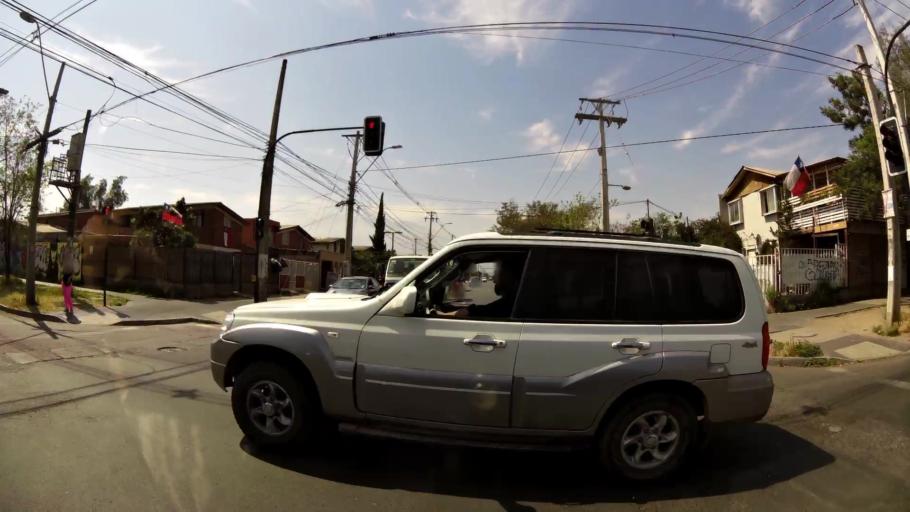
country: CL
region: Santiago Metropolitan
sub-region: Provincia de Cordillera
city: Puente Alto
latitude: -33.5876
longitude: -70.5965
